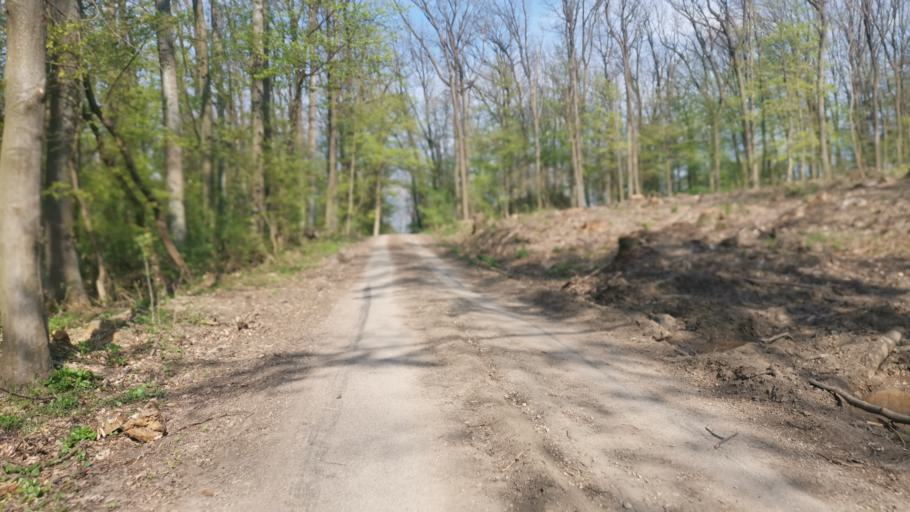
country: SK
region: Trnavsky
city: Smolenice
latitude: 48.5727
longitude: 17.3870
